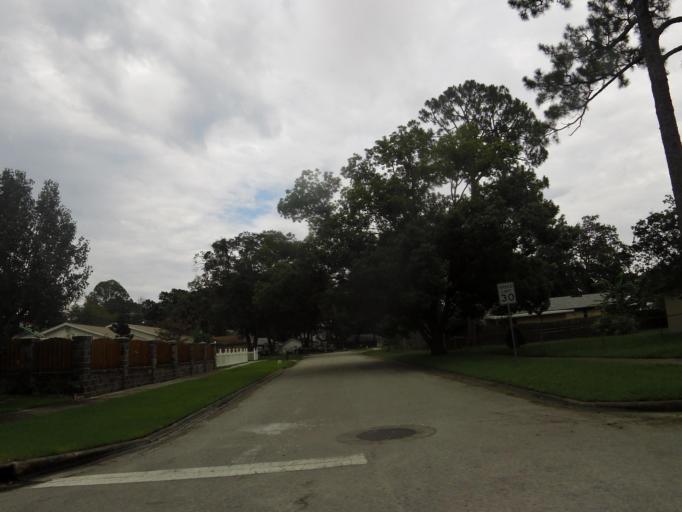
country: US
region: Florida
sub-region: Duval County
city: Jacksonville Beach
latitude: 30.2783
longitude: -81.4337
